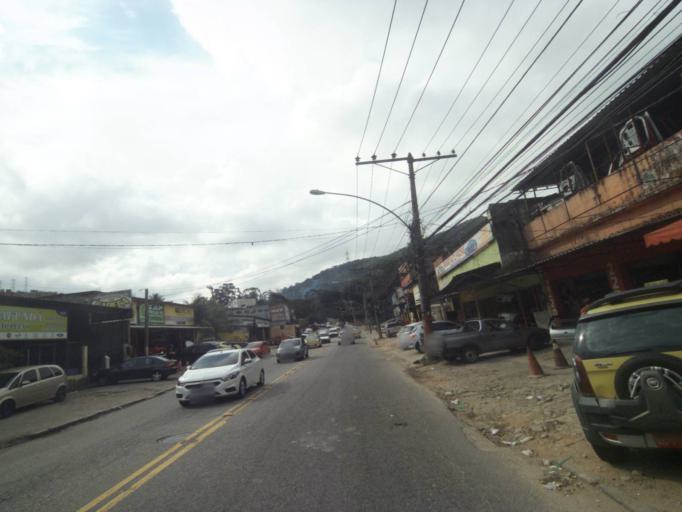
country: BR
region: Rio de Janeiro
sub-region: Sao Joao De Meriti
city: Sao Joao de Meriti
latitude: -22.9096
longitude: -43.3786
